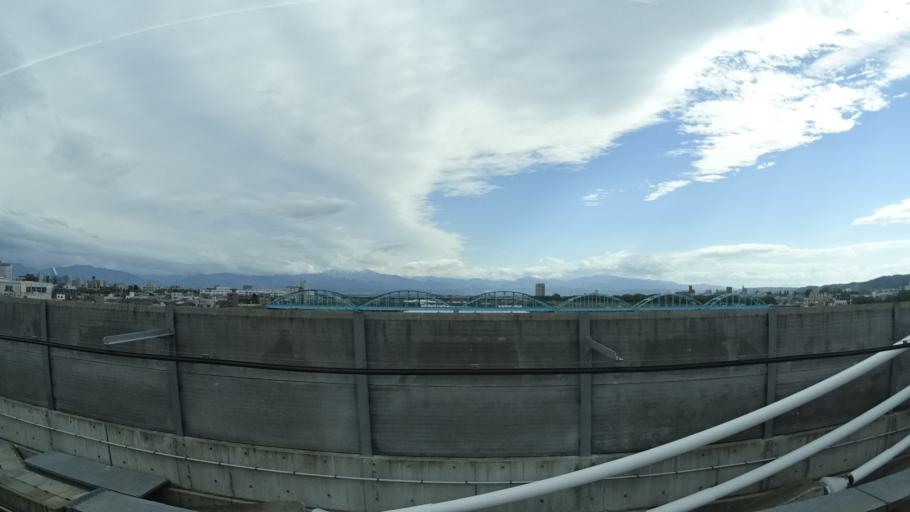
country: JP
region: Toyama
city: Toyama-shi
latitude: 36.7051
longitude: 137.2042
